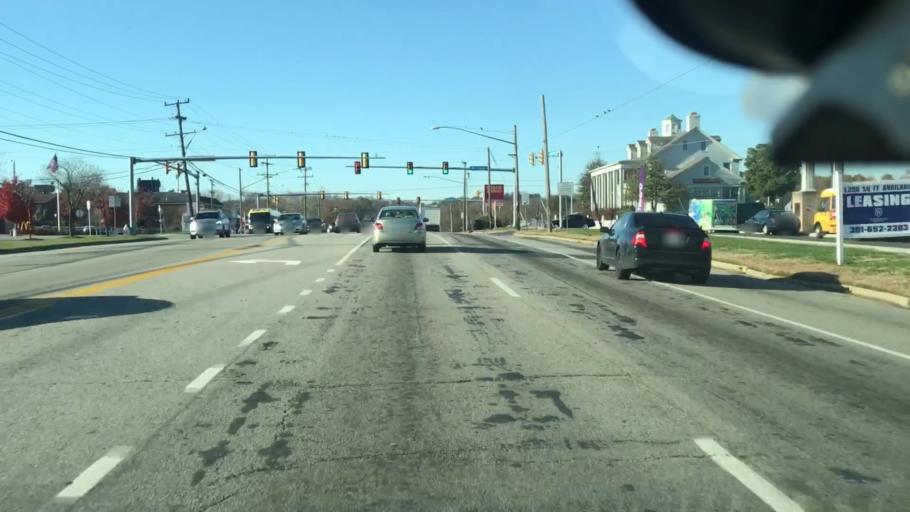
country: US
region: Virginia
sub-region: Fairfax County
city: Woodlawn
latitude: 38.7211
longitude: -77.1242
